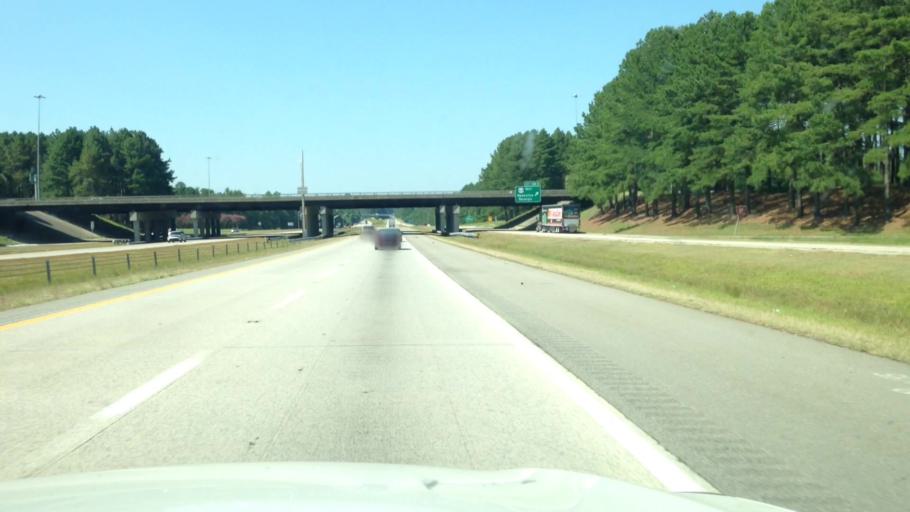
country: US
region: North Carolina
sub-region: Nash County
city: Red Oak
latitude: 35.9803
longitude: -77.8768
